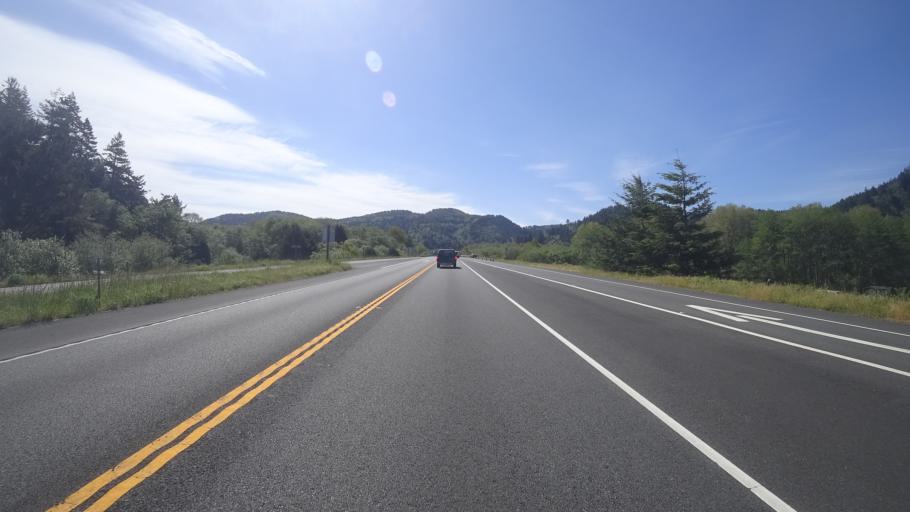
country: US
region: California
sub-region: Del Norte County
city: Bertsch-Oceanview
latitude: 41.5218
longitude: -124.0333
